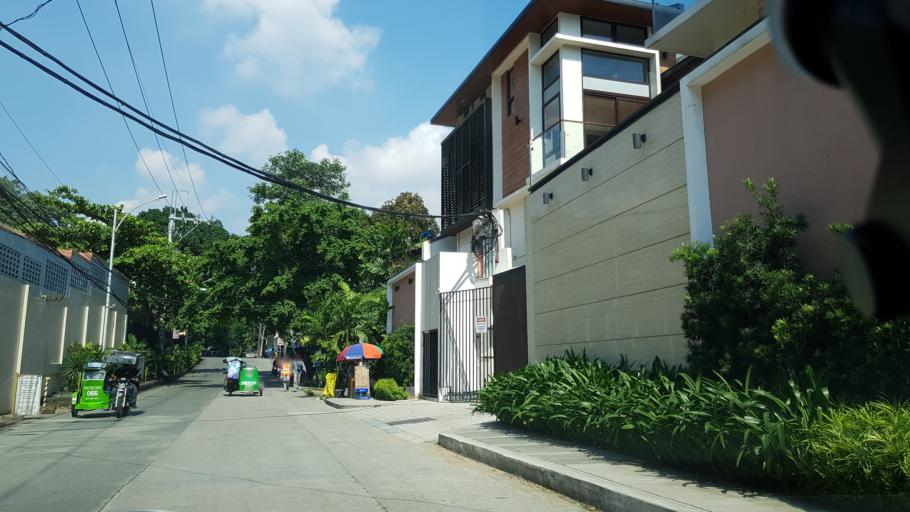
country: PH
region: Metro Manila
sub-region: San Juan
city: San Juan
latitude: 14.6139
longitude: 121.0306
